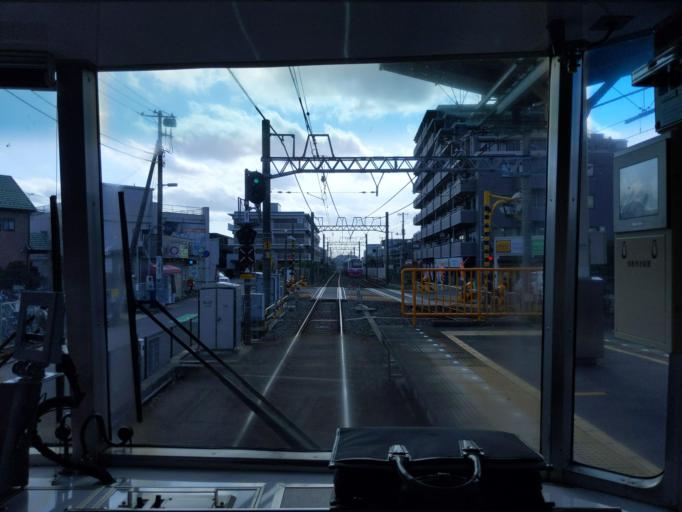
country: JP
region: Chiba
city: Funabashi
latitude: 35.7101
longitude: 140.0379
